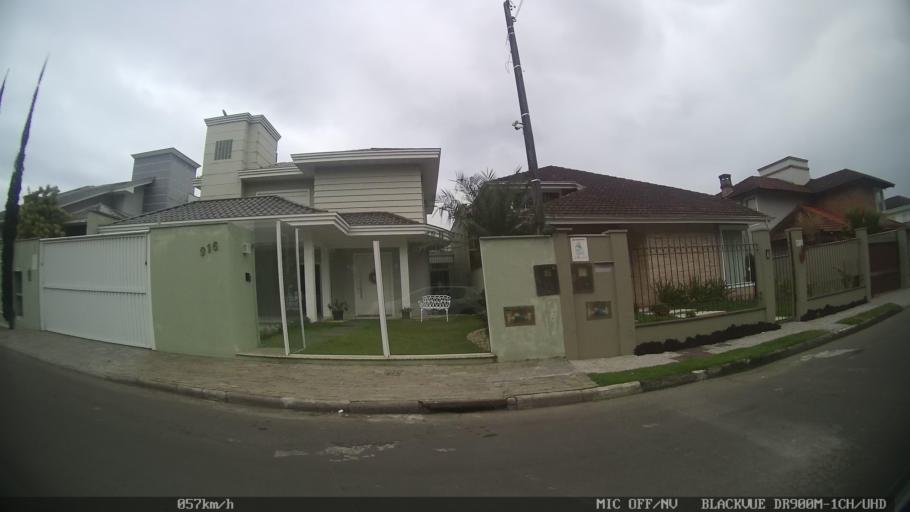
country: BR
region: Santa Catarina
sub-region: Joinville
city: Joinville
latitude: -26.2720
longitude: -48.8655
